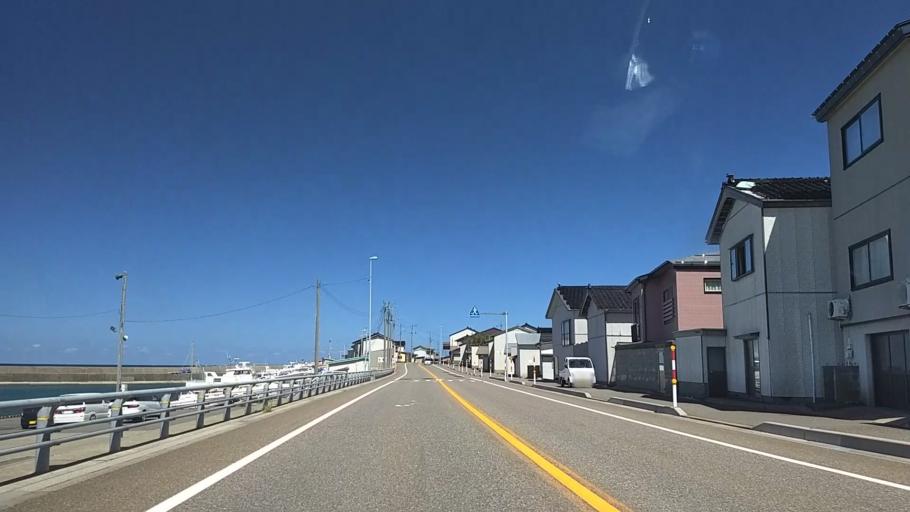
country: JP
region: Niigata
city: Joetsu
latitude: 37.1665
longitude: 138.0895
